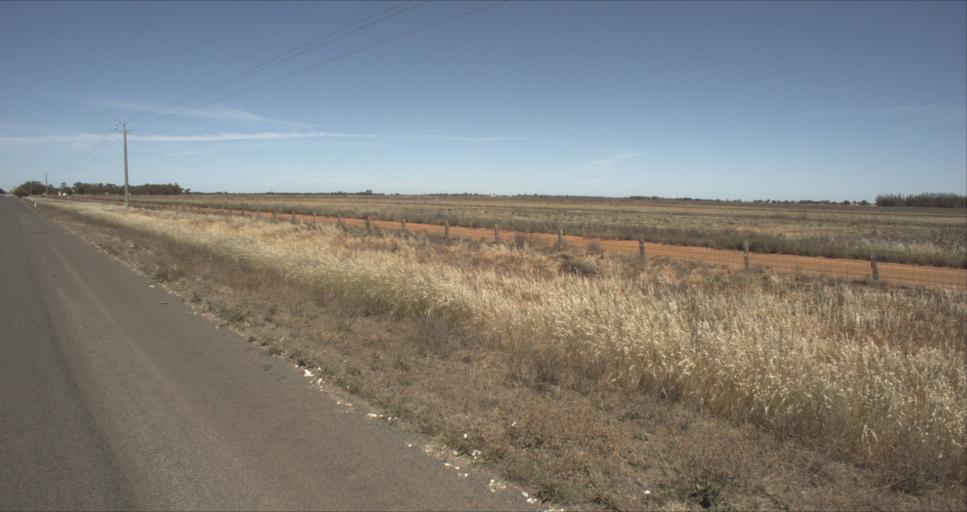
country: AU
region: New South Wales
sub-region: Leeton
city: Leeton
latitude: -34.4878
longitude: 146.2893
